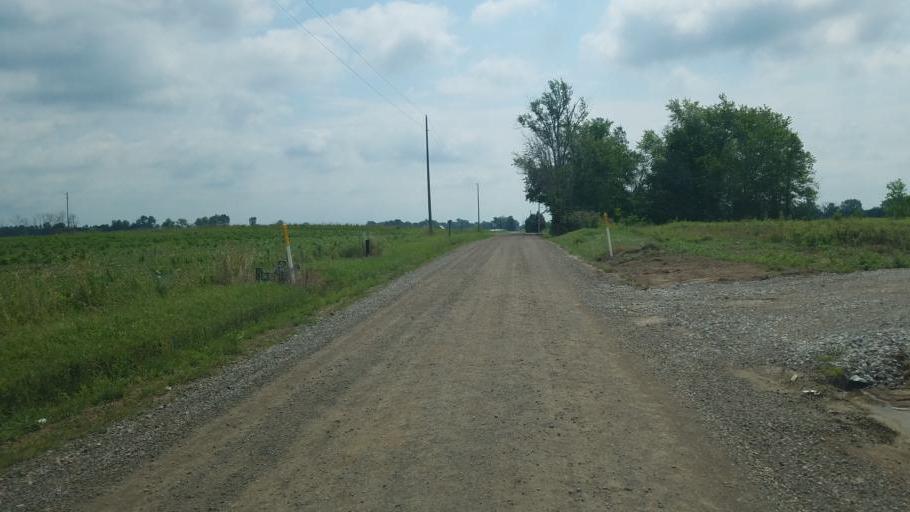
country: US
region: Ohio
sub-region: Knox County
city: Centerburg
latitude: 40.2916
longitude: -82.5743
